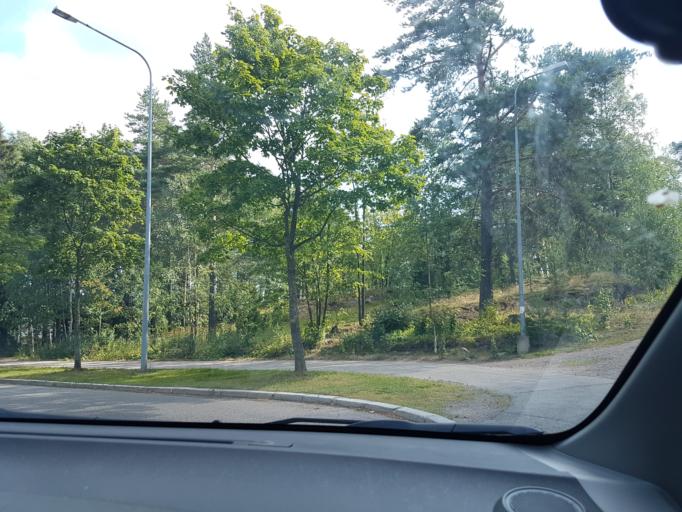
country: FI
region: Uusimaa
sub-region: Helsinki
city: Vantaa
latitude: 60.2284
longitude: 25.0563
